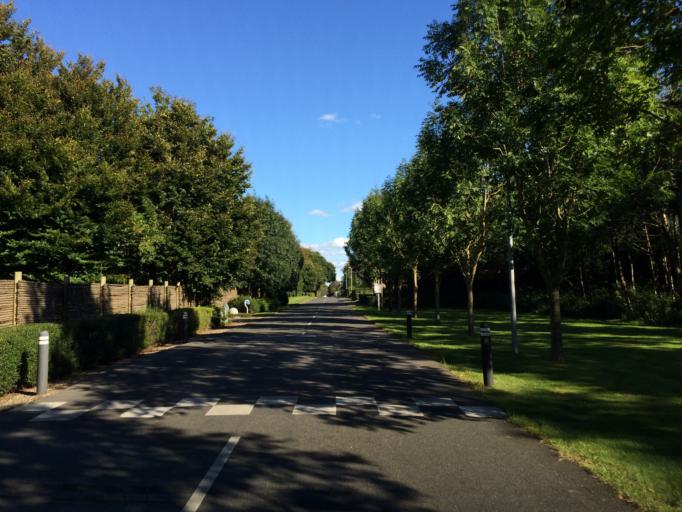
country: DK
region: Central Jutland
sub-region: Holstebro Kommune
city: Holstebro
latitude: 56.3231
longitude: 8.6947
